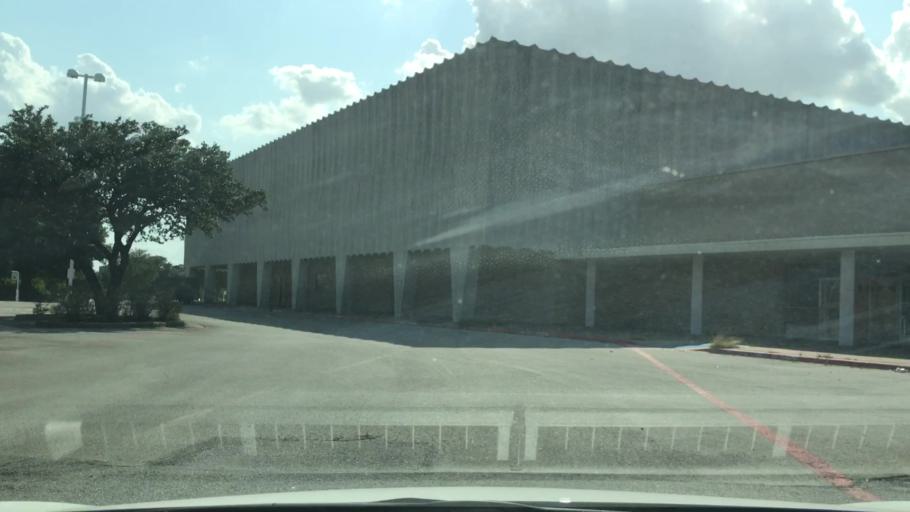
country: US
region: Texas
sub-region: Dallas County
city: Addison
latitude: 32.9281
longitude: -96.8060
